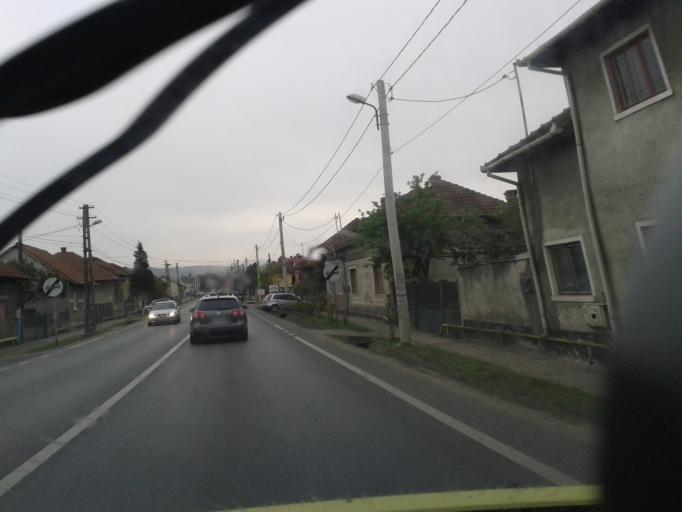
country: RO
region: Hunedoara
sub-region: Oras Simeria
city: Simeria
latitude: 45.8433
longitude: 23.0148
